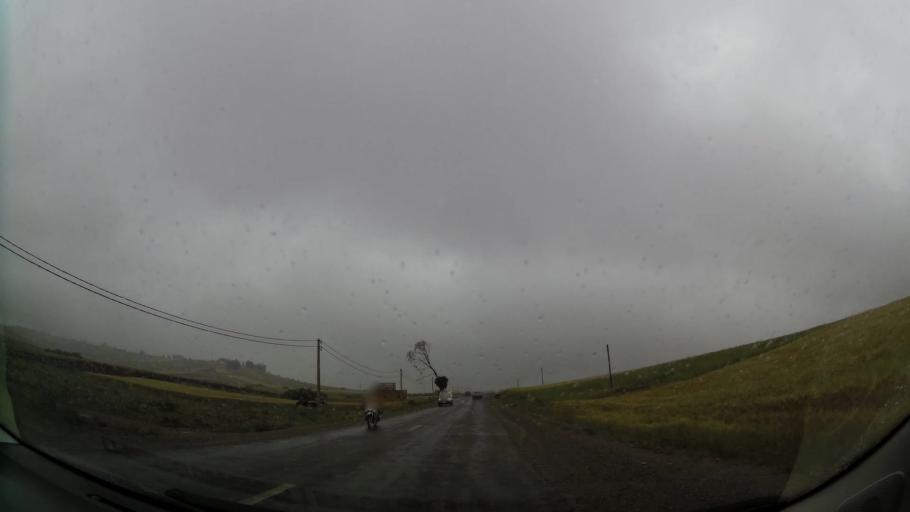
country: MA
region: Oriental
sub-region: Nador
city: Boudinar
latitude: 35.1382
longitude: -3.6203
